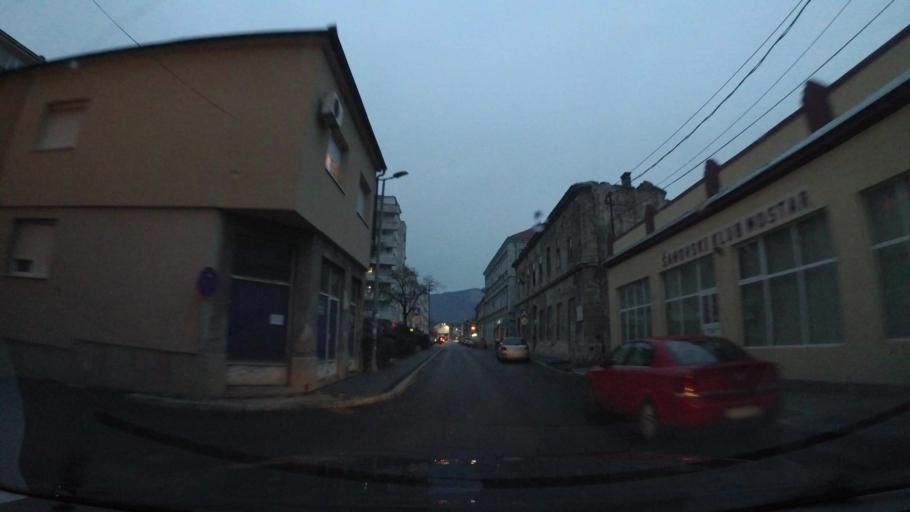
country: BA
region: Federation of Bosnia and Herzegovina
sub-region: Hercegovacko-Bosanski Kanton
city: Mostar
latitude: 43.3422
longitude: 17.8144
